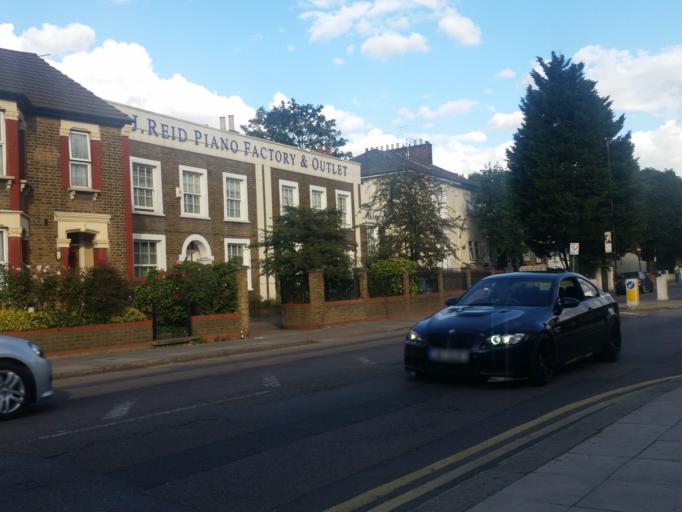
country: GB
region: England
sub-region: Greater London
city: Harringay
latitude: 51.5804
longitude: -0.0830
